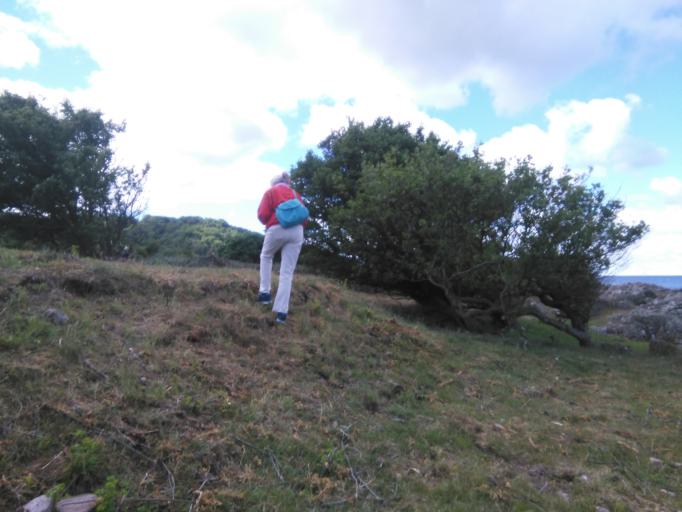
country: DK
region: Capital Region
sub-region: Bornholm Kommune
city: Ronne
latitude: 55.2944
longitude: 14.7644
